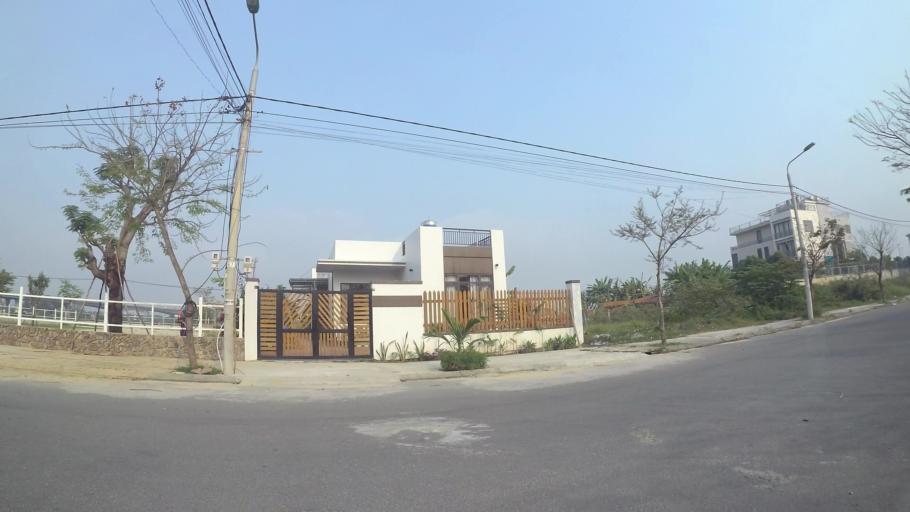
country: VN
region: Da Nang
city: Cam Le
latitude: 16.0147
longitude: 108.2176
